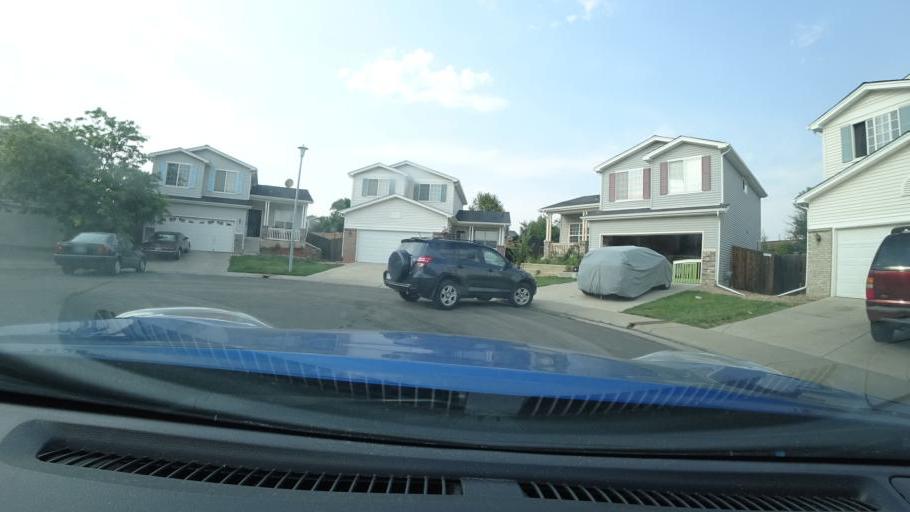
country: US
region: Colorado
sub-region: Adams County
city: Aurora
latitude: 39.7464
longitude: -104.7591
